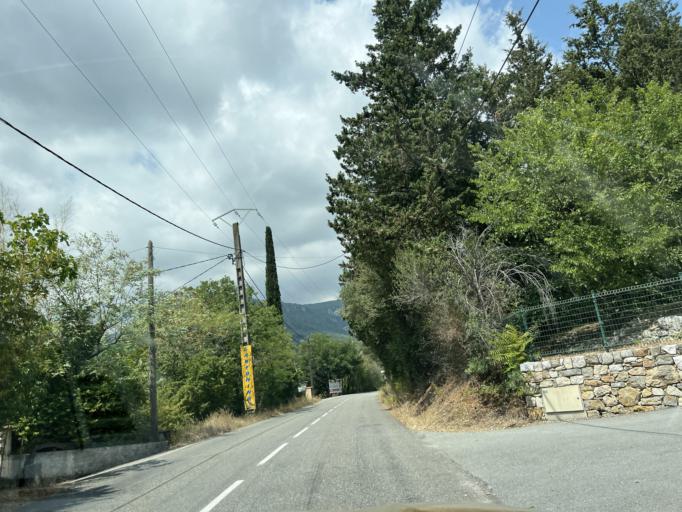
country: FR
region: Provence-Alpes-Cote d'Azur
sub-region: Departement des Alpes-Maritimes
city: Le Rouret
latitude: 43.6989
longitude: 7.0091
